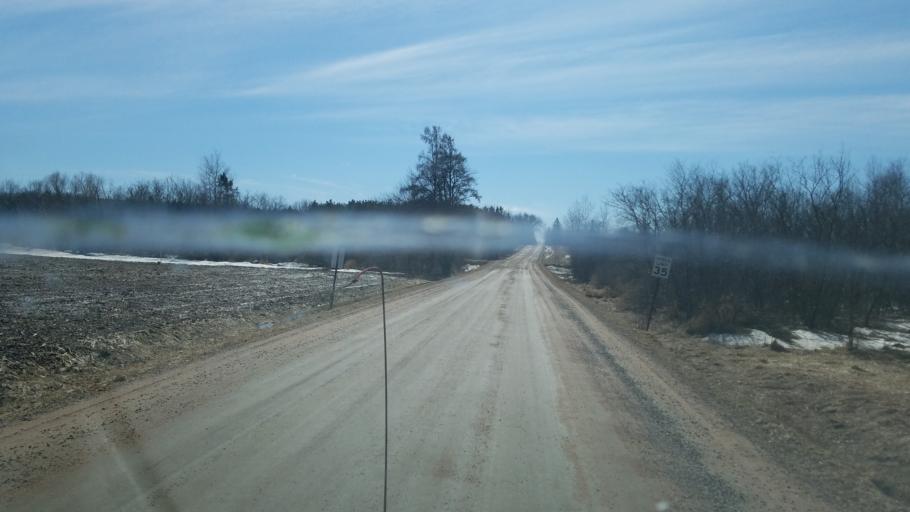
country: US
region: Wisconsin
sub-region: Clark County
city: Neillsville
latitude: 44.5913
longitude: -90.4564
